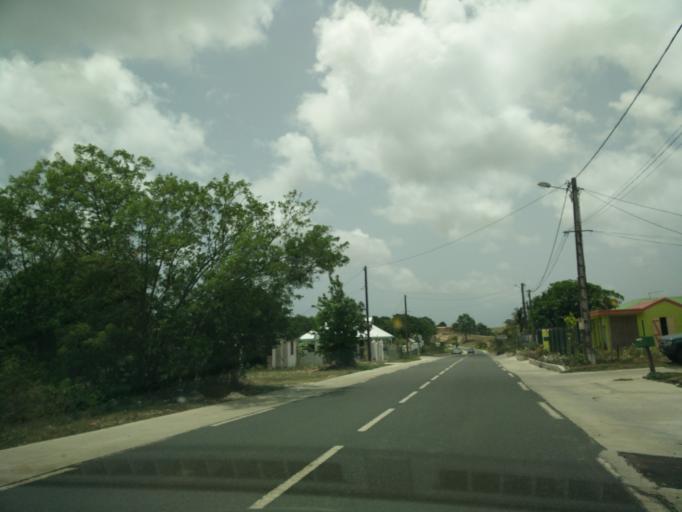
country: GP
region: Guadeloupe
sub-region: Guadeloupe
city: Port-Louis
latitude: 16.4248
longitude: -61.5198
